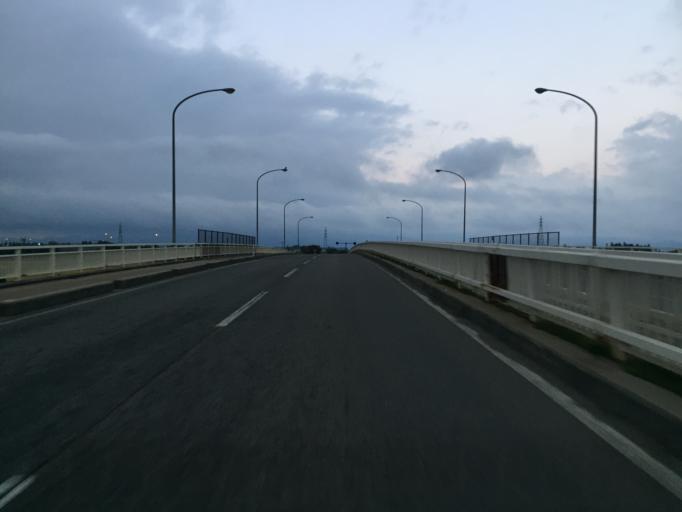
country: JP
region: Fukushima
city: Inawashiro
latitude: 37.5458
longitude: 140.1114
